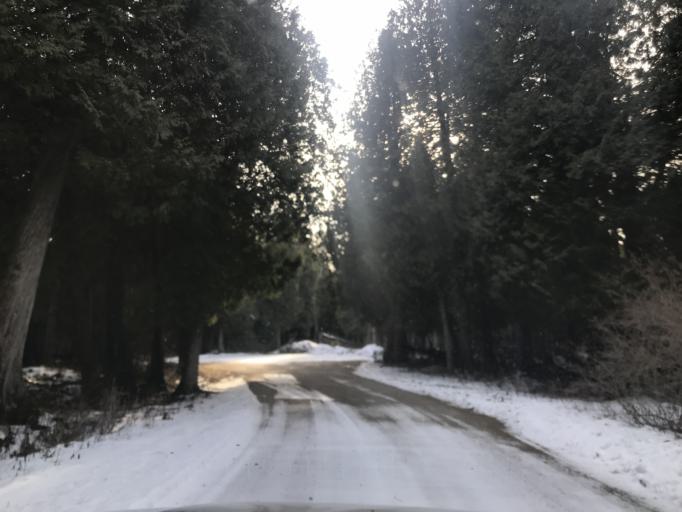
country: US
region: Wisconsin
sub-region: Door County
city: Sturgeon Bay
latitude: 45.1470
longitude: -87.0320
